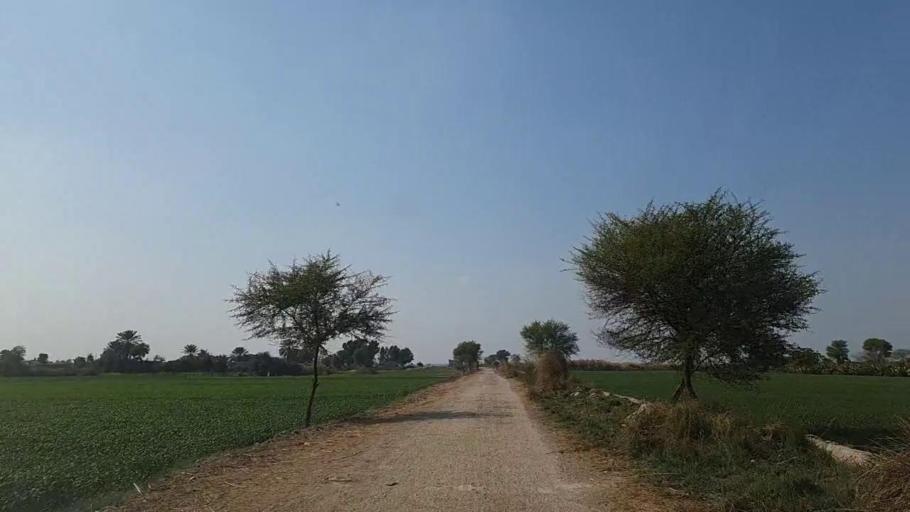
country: PK
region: Sindh
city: Daur
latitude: 26.4961
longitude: 68.2679
